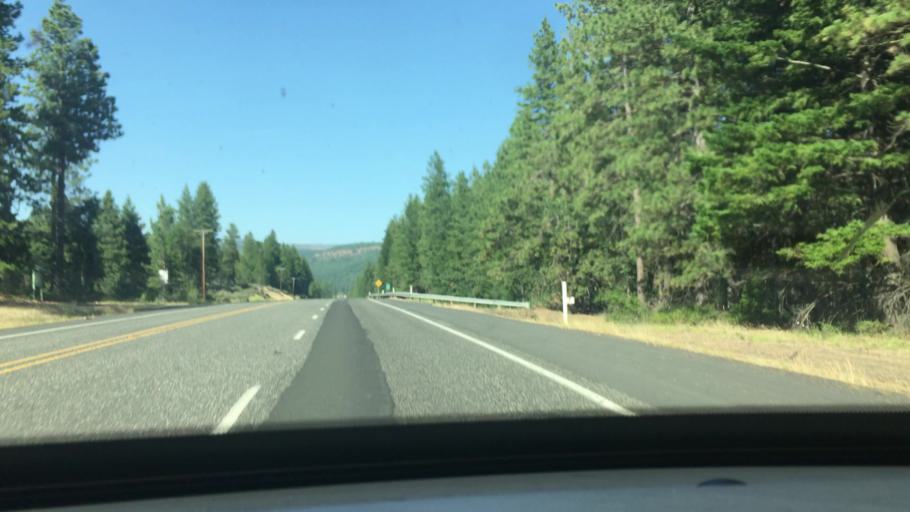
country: US
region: Washington
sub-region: Klickitat County
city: Goldendale
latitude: 45.9340
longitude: -120.6939
